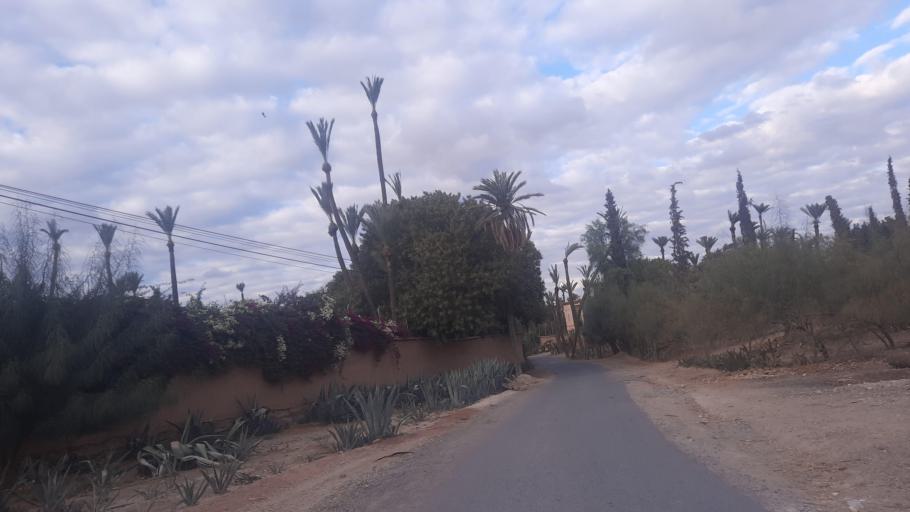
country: MA
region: Marrakech-Tensift-Al Haouz
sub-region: Marrakech
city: Marrakesh
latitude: 31.6735
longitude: -7.9536
